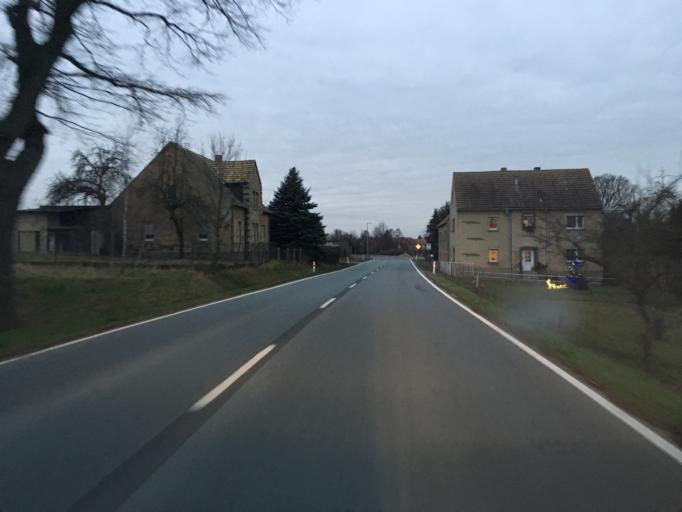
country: DE
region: Saxony
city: Dahlen
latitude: 51.3270
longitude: 13.0160
